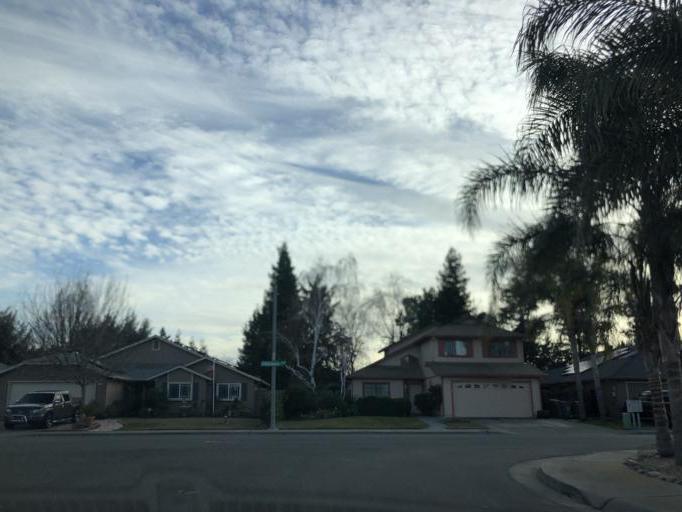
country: US
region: California
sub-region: Yolo County
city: Woodland
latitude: 38.6691
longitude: -121.7531
